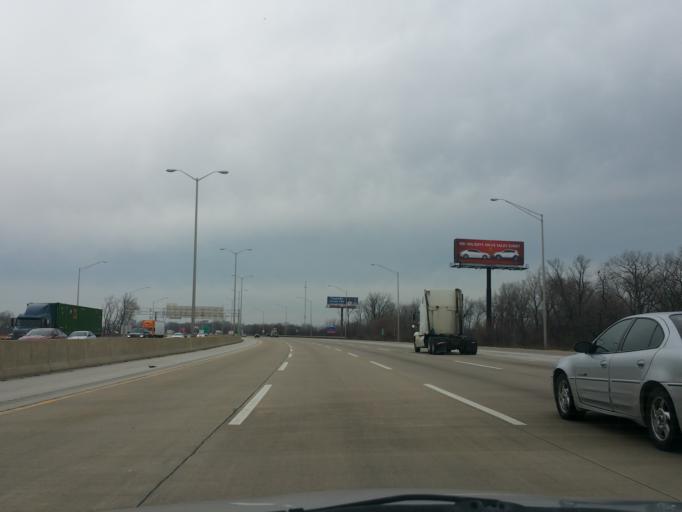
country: US
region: Illinois
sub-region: Cook County
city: University Park
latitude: 41.6050
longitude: -87.6811
